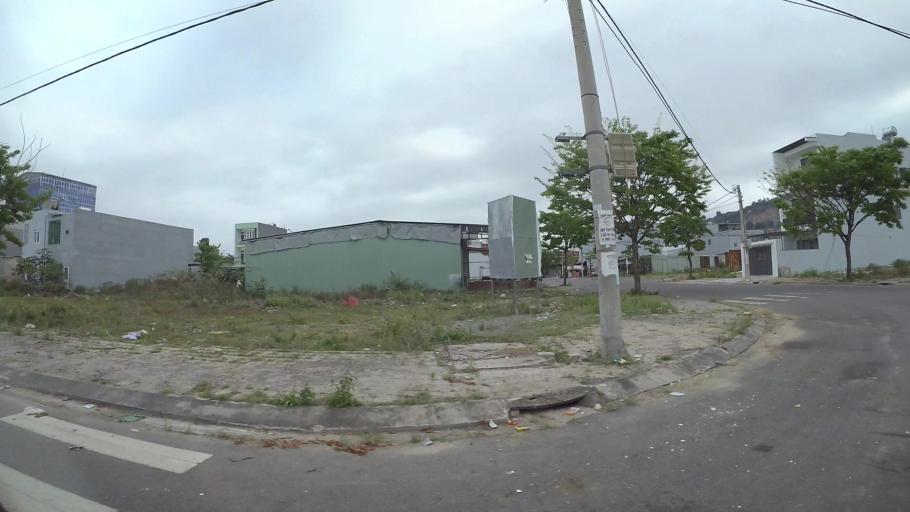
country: VN
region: Da Nang
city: Lien Chieu
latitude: 16.0482
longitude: 108.1653
